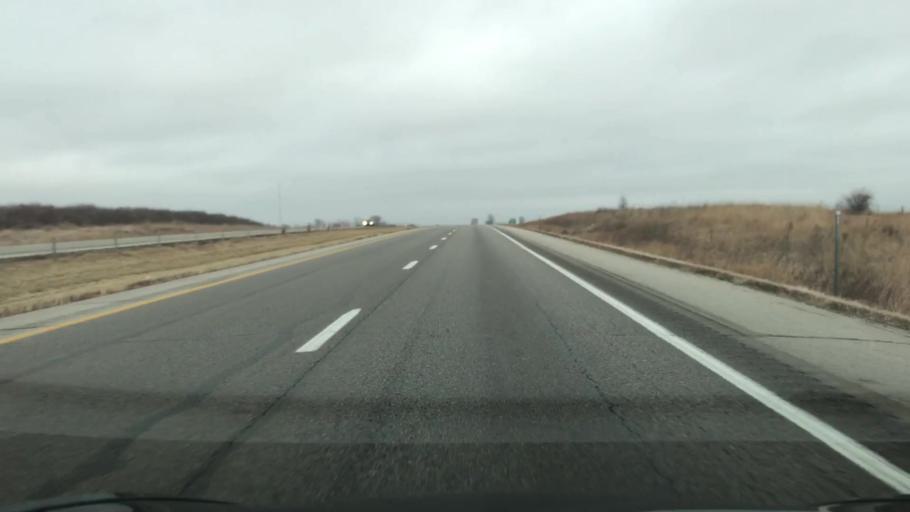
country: US
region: Iowa
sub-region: Madison County
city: Earlham
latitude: 41.4971
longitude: -94.2169
